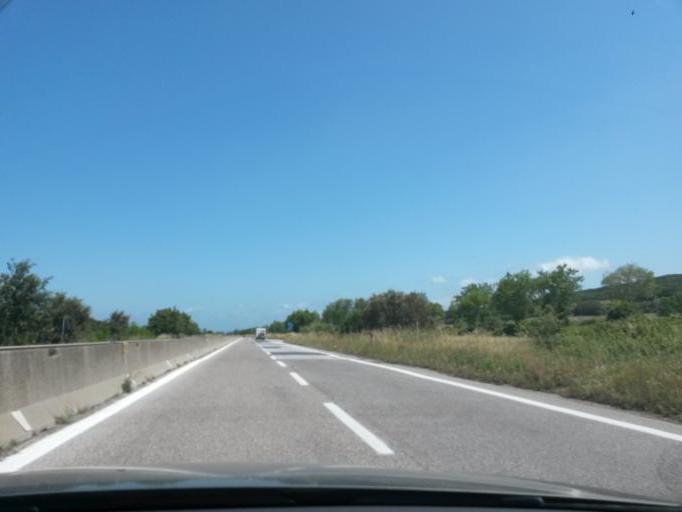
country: IT
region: Tuscany
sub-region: Provincia di Livorno
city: San Vincenzo
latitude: 43.1268
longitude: 10.5469
